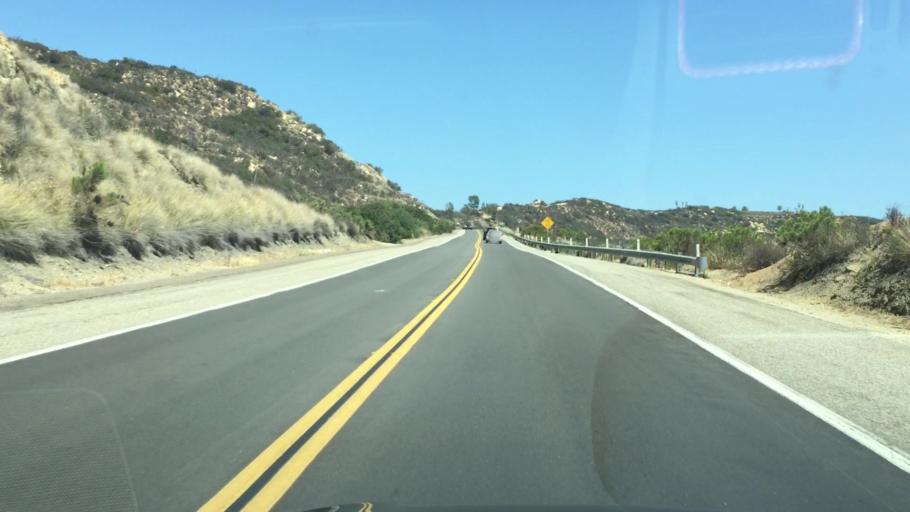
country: US
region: California
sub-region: San Diego County
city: Jamul
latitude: 32.7343
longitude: -116.8364
